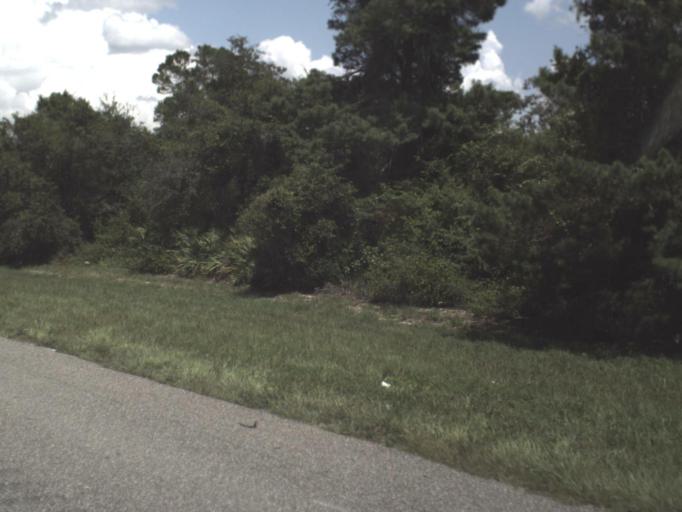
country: US
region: Florida
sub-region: Hillsborough County
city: Riverview
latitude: 27.8401
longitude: -82.3483
